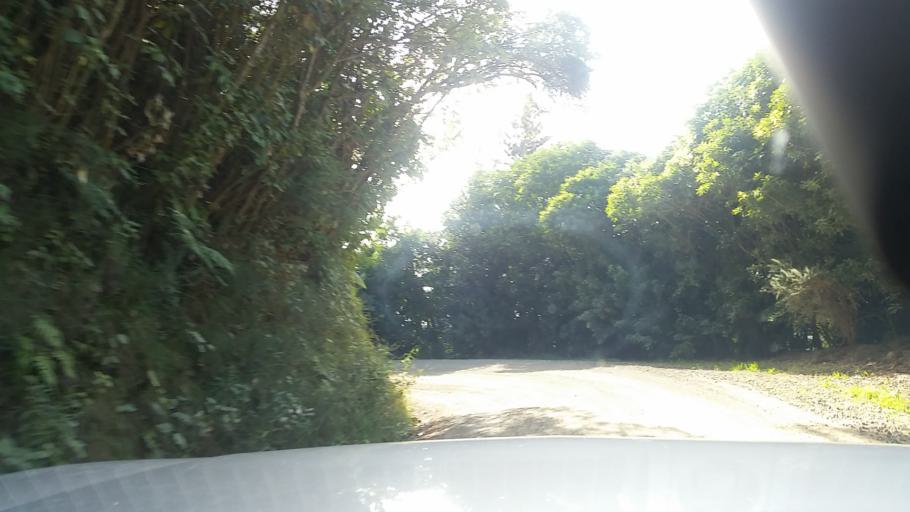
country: NZ
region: Marlborough
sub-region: Marlborough District
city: Picton
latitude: -41.2960
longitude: 174.1237
